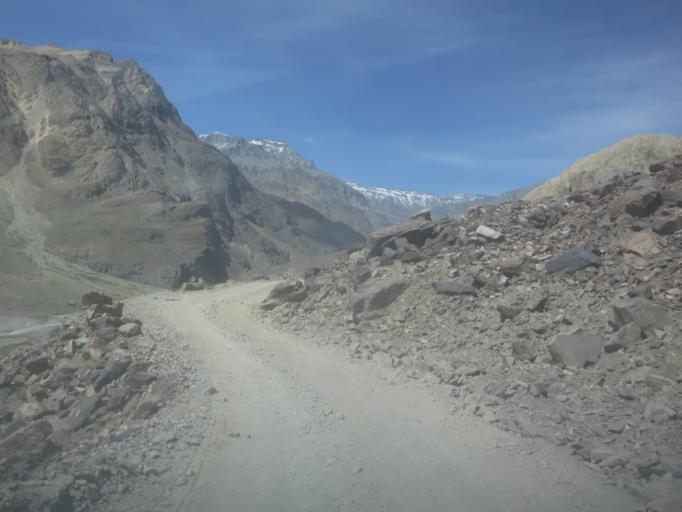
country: IN
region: Himachal Pradesh
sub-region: Kulu
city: Manali
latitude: 32.4262
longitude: 77.6688
